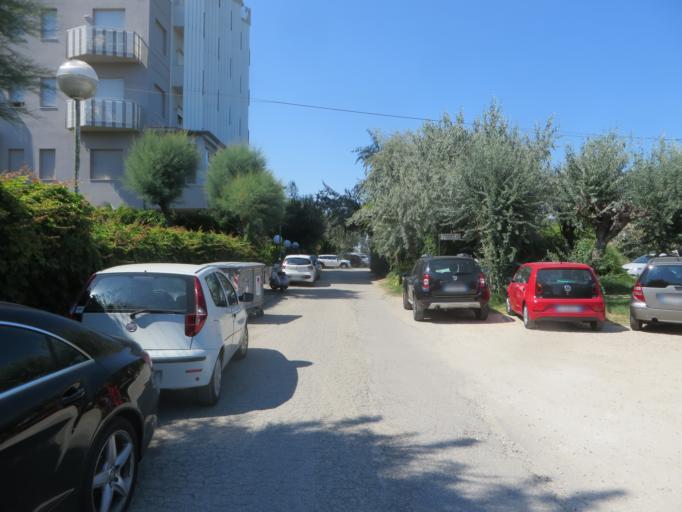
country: IT
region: Emilia-Romagna
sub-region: Provincia di Ravenna
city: Cervia
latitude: 44.2690
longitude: 12.3559
